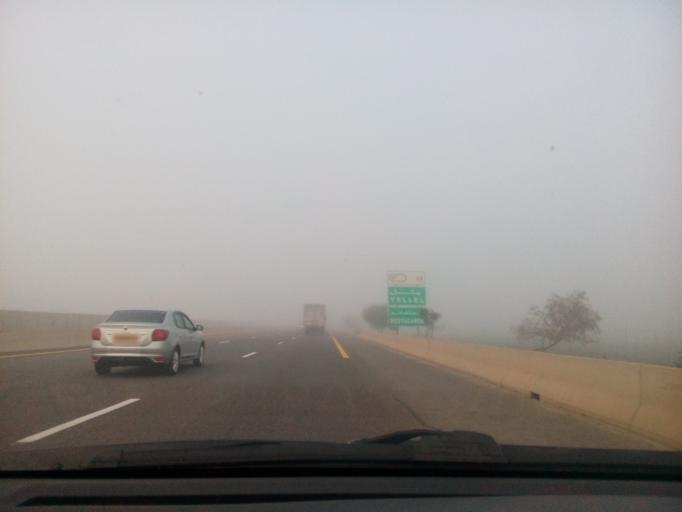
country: DZ
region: Relizane
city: Relizane
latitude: 35.7977
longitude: 0.5267
